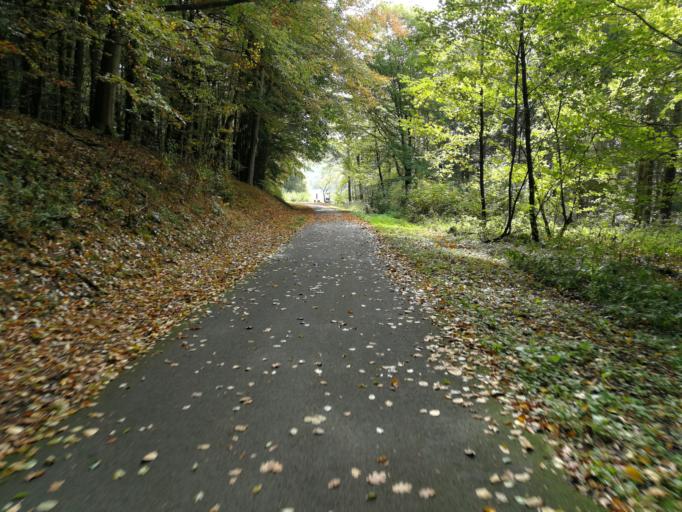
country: DE
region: North Rhine-Westphalia
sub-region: Regierungsbezirk Arnsberg
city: Meschede
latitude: 51.3201
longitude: 8.2723
